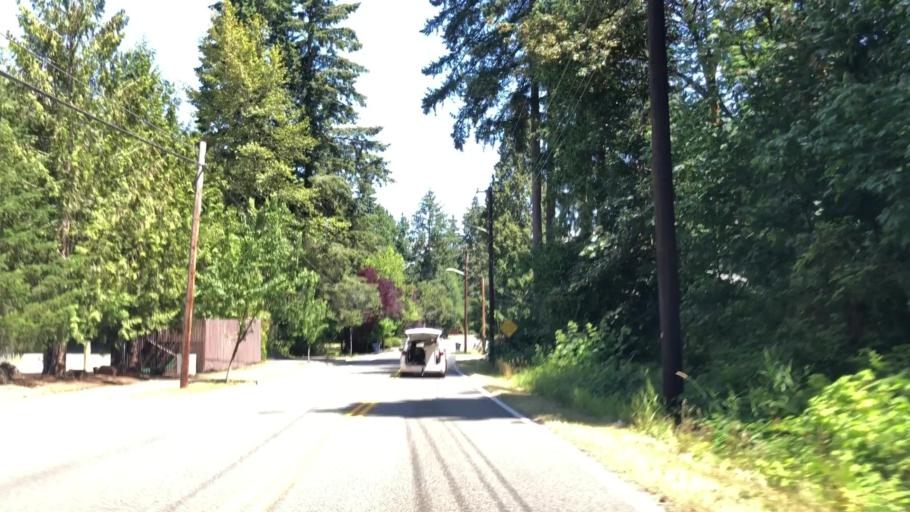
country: US
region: Washington
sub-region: Snohomish County
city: North Creek
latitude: 47.8192
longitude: -122.1786
